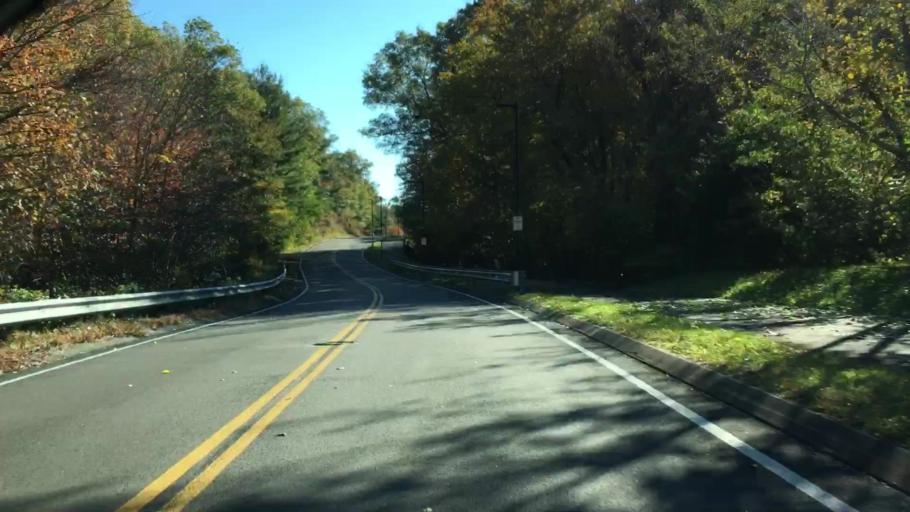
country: US
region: Massachusetts
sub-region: Middlesex County
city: Ashland
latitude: 42.2541
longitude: -71.4742
